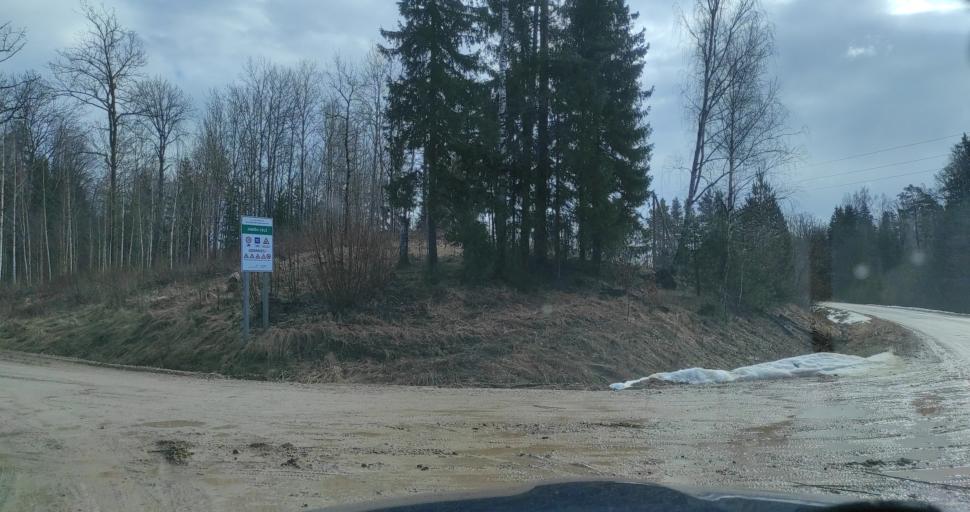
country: LV
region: Tukuma Rajons
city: Tukums
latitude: 57.1062
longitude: 23.0393
